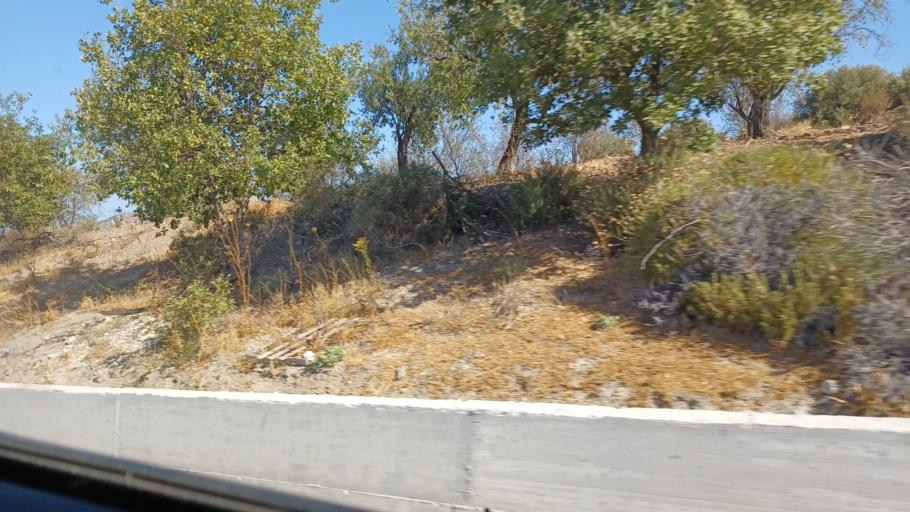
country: CY
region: Pafos
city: Polis
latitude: 34.9471
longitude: 32.4971
